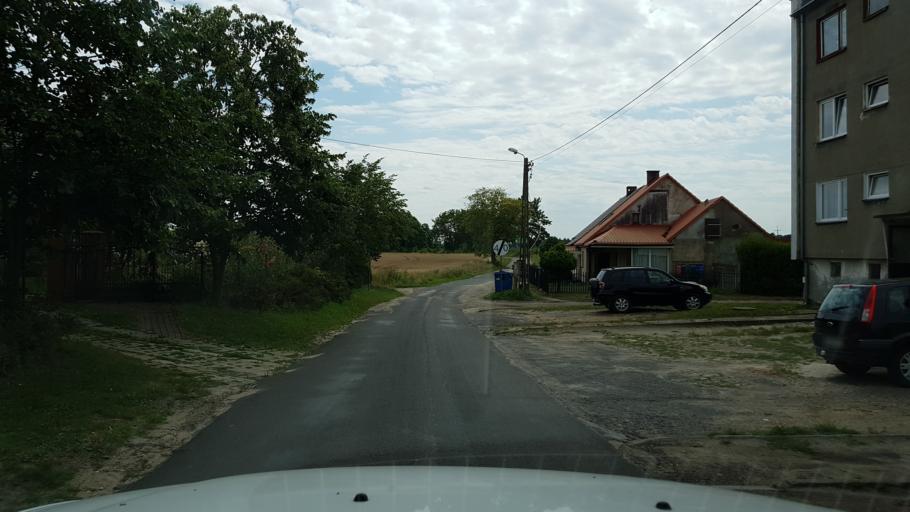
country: PL
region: West Pomeranian Voivodeship
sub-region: Powiat koszalinski
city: Mielno
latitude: 54.1695
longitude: 16.0550
